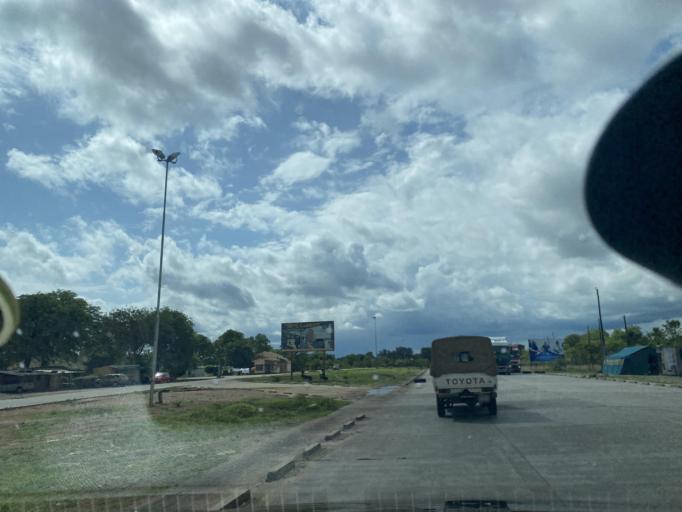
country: ZM
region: Lusaka
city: Kafue
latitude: -15.8460
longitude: 28.2443
